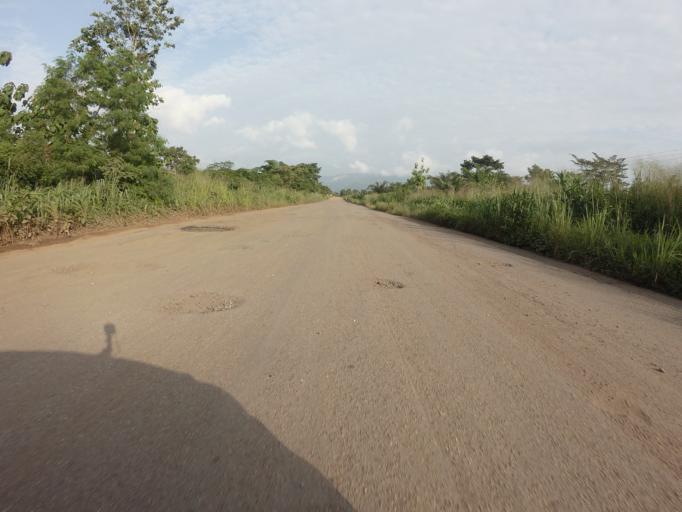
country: GH
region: Volta
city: Kpandu
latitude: 6.9720
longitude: 0.4525
